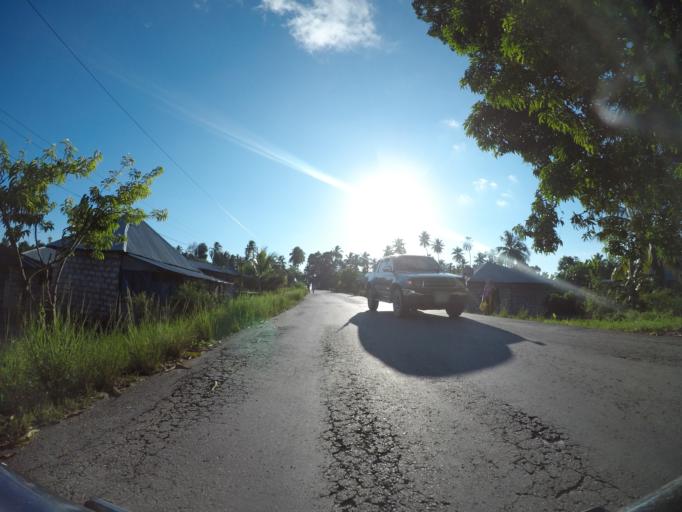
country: TZ
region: Pemba South
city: Mtambile
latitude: -5.3684
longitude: 39.7101
